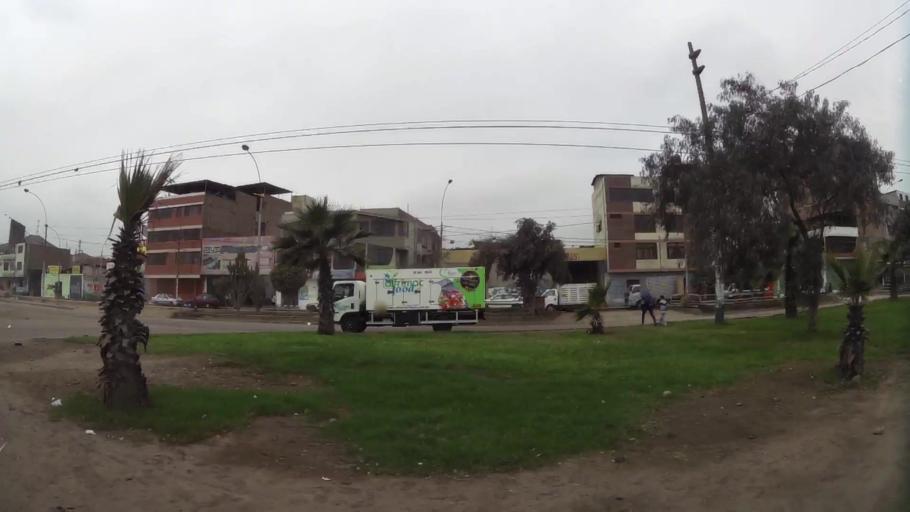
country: PE
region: Lima
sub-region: Lima
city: Independencia
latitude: -12.0078
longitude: -77.0822
